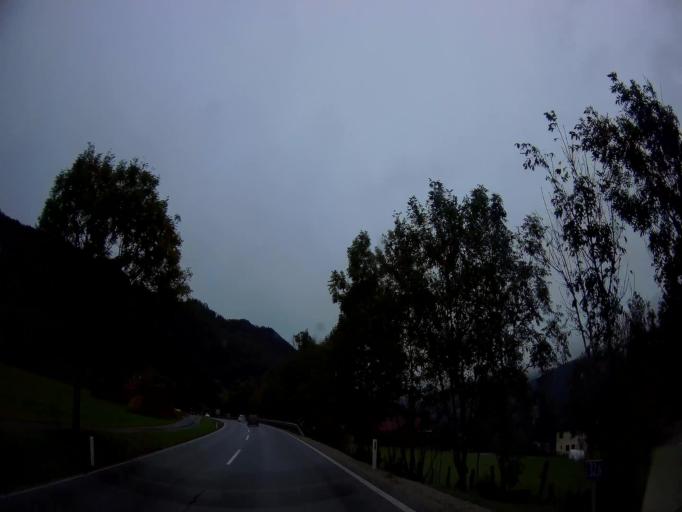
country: AT
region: Styria
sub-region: Politischer Bezirk Liezen
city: Pruggern
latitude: 47.4237
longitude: 13.8651
